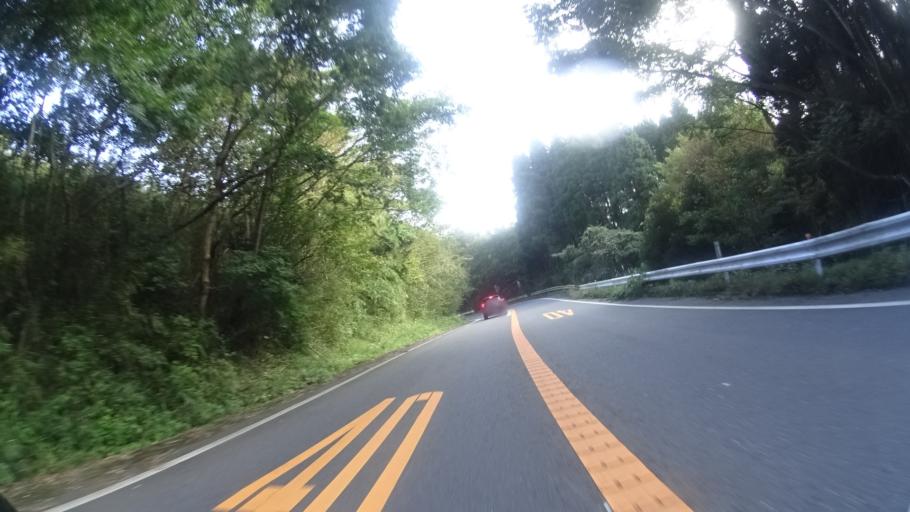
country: JP
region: Oita
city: Beppu
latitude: 33.2709
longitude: 131.4287
